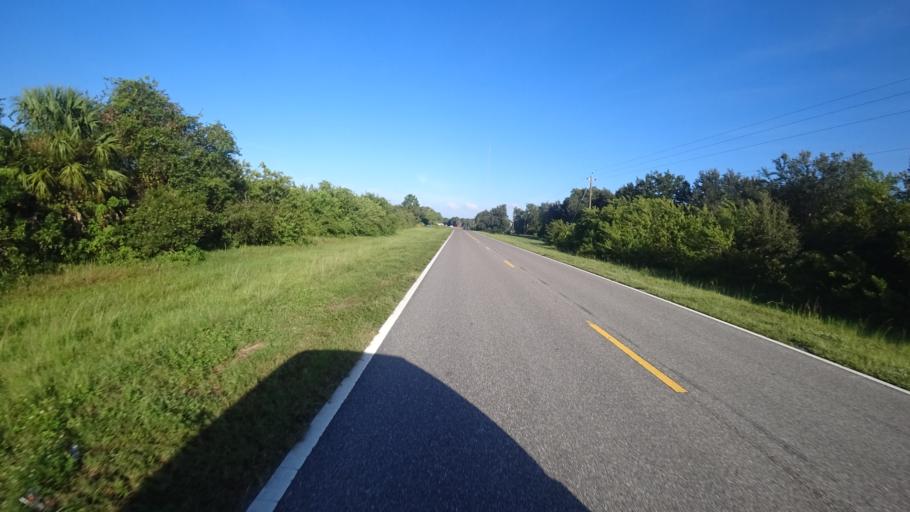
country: US
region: Florida
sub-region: Hillsborough County
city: Sun City Center
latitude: 27.5509
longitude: -82.3596
